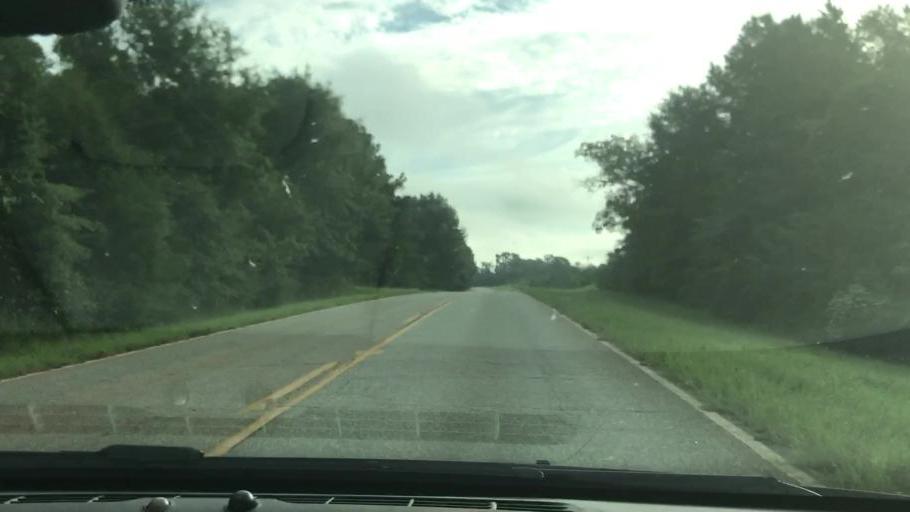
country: US
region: Georgia
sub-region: Quitman County
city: Georgetown
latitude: 31.9006
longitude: -85.0458
